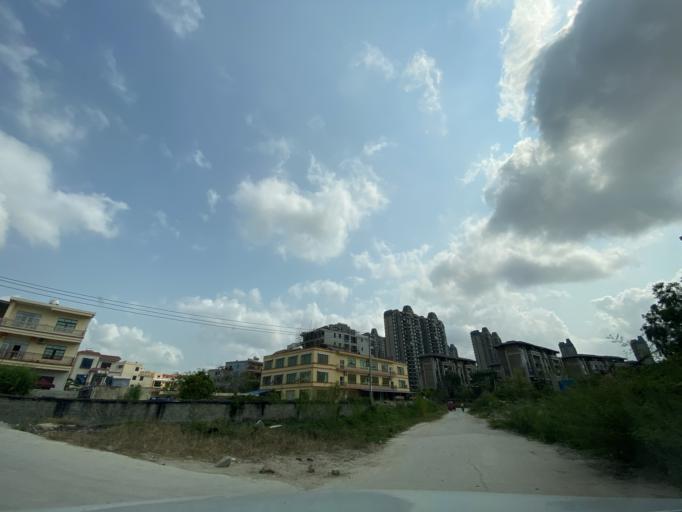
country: CN
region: Hainan
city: Yingzhou
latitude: 18.4166
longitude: 109.8478
